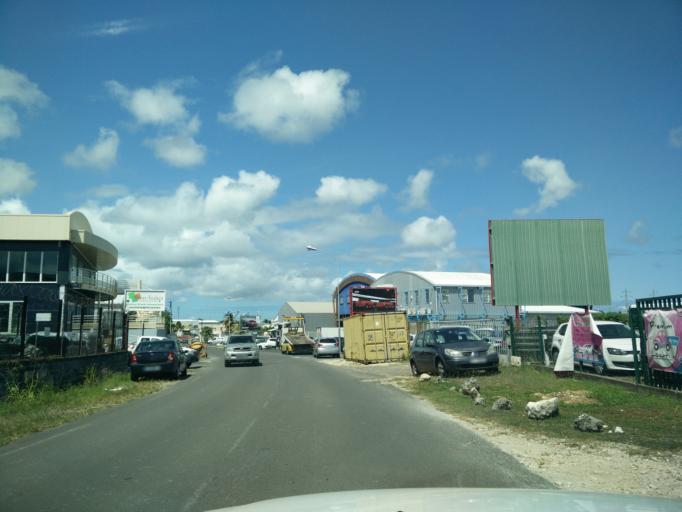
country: GP
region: Guadeloupe
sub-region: Guadeloupe
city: Pointe-a-Pitre
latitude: 16.2385
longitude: -61.5660
